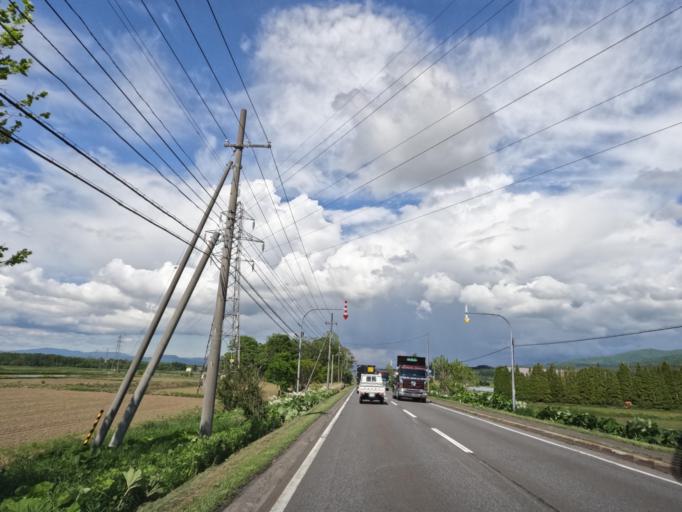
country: JP
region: Hokkaido
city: Fukagawa
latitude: 43.6655
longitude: 142.0004
